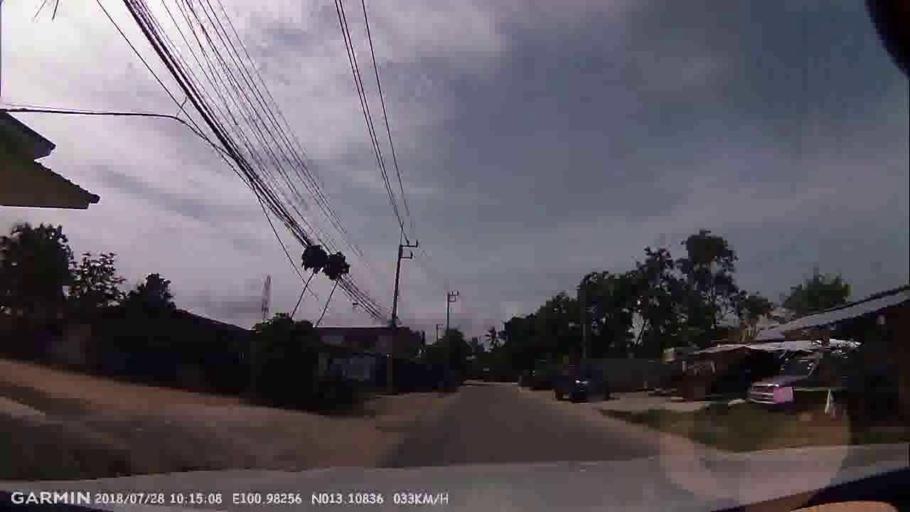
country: TH
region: Chon Buri
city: Ban Talat Bueng
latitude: 13.1083
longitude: 100.9826
